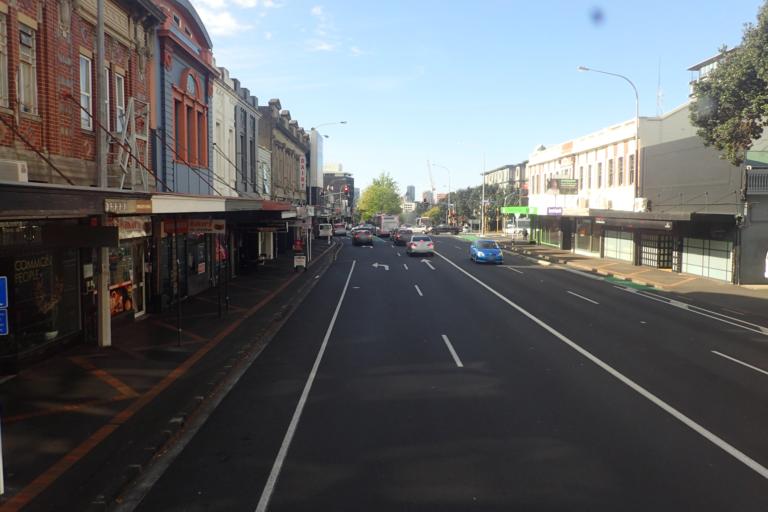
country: NZ
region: Auckland
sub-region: Auckland
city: Auckland
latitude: -36.8646
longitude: 174.7607
